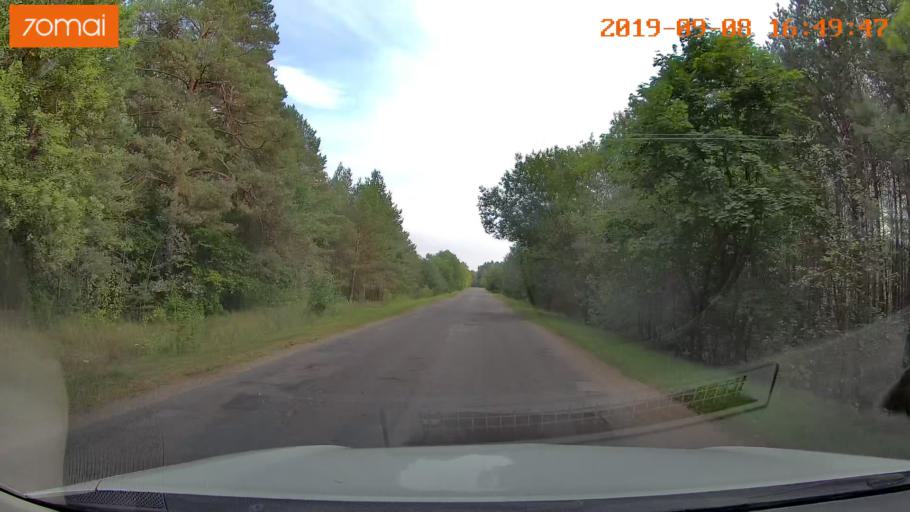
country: BY
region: Grodnenskaya
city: Hrodna
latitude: 53.8071
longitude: 23.8793
